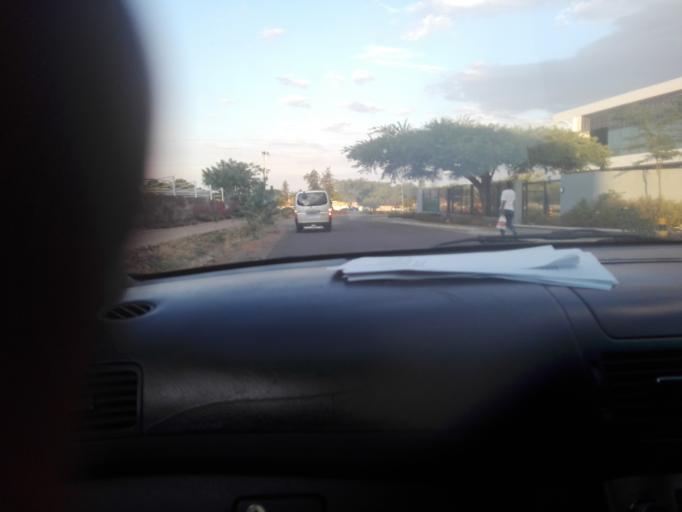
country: BW
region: South East
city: Gaborone
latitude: -24.6848
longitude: 25.8790
